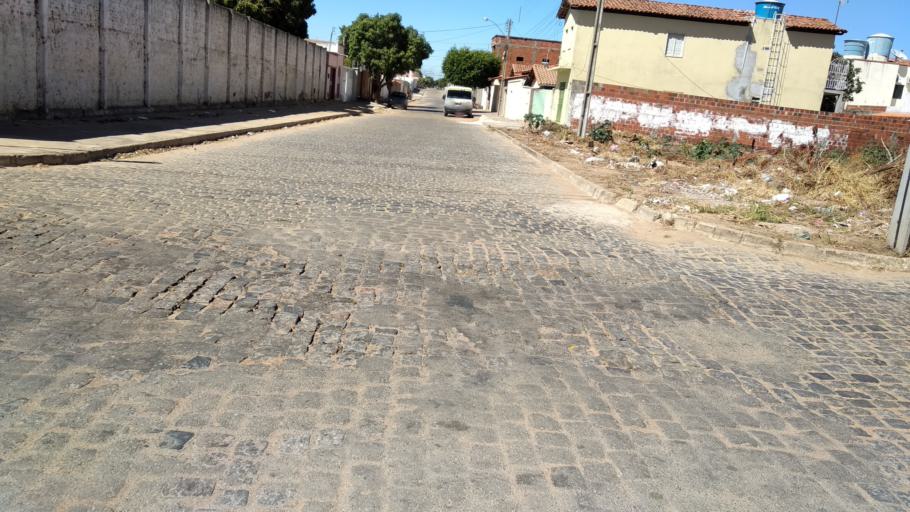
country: BR
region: Bahia
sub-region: Guanambi
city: Guanambi
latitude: -14.2336
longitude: -42.7766
